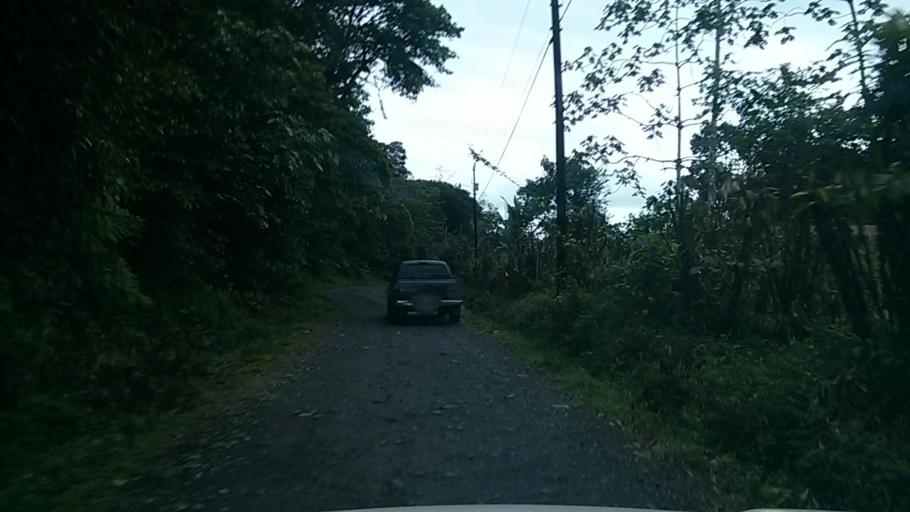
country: CR
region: Limon
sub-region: Canton de Pococi
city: Guapiles
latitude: 10.1679
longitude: -83.7833
